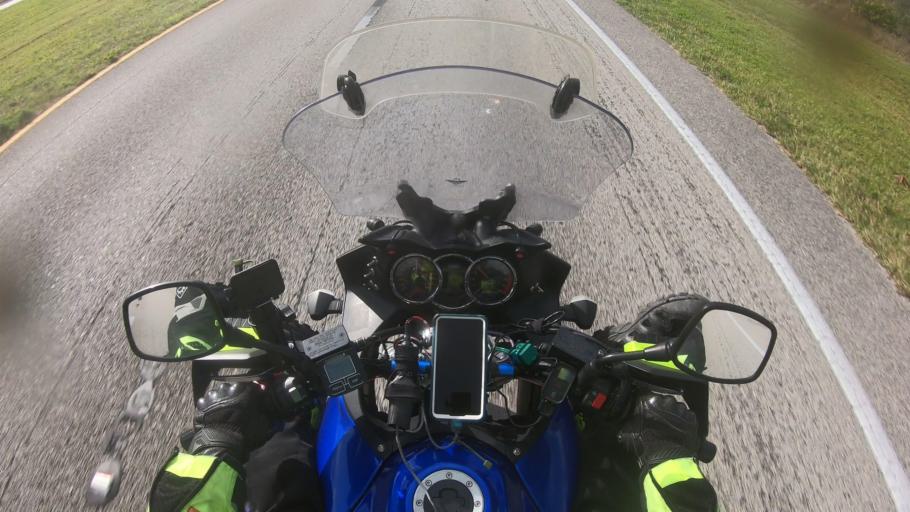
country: US
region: Florida
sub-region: Hendry County
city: Port LaBelle
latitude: 26.9126
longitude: -81.2817
